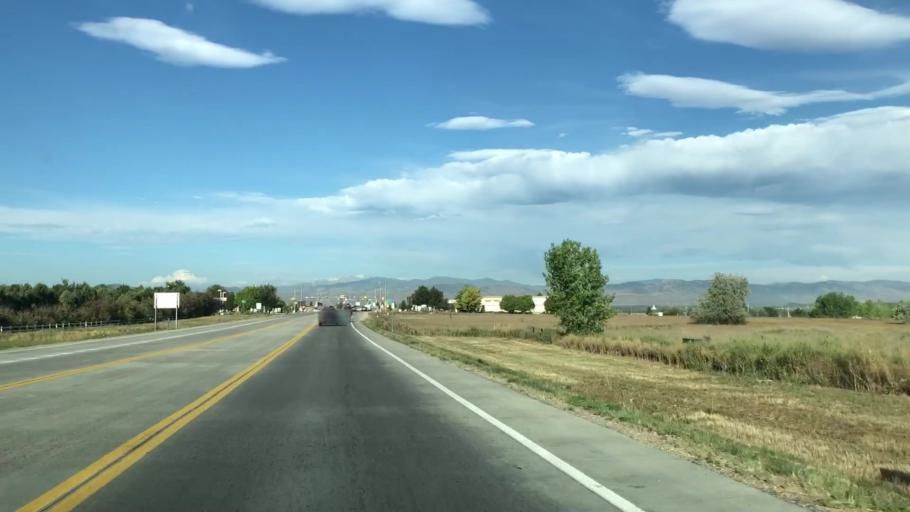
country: US
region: Colorado
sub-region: Weld County
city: Windsor
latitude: 40.4796
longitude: -104.9843
